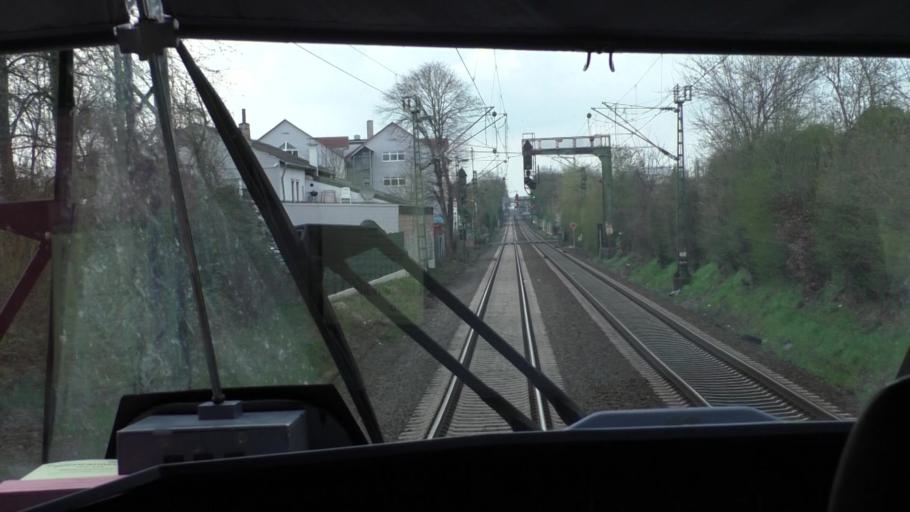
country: DE
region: North Rhine-Westphalia
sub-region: Regierungsbezirk Koln
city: Konigswinter
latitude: 50.6754
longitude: 7.1727
